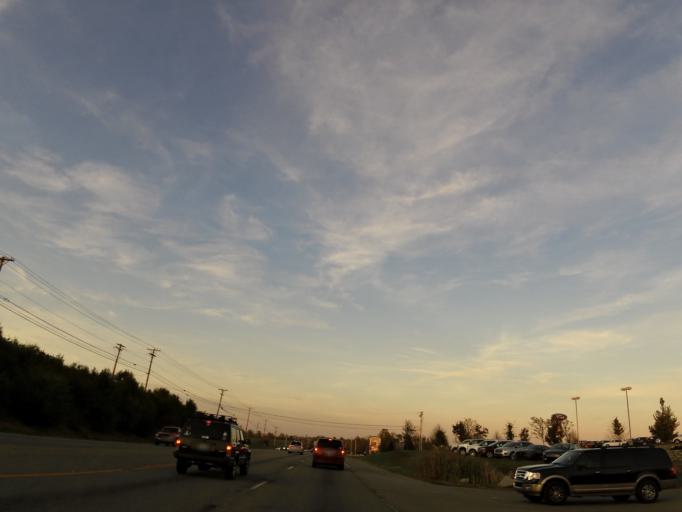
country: US
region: Kentucky
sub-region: Fayette County
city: Monticello
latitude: 37.9542
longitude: -84.5401
